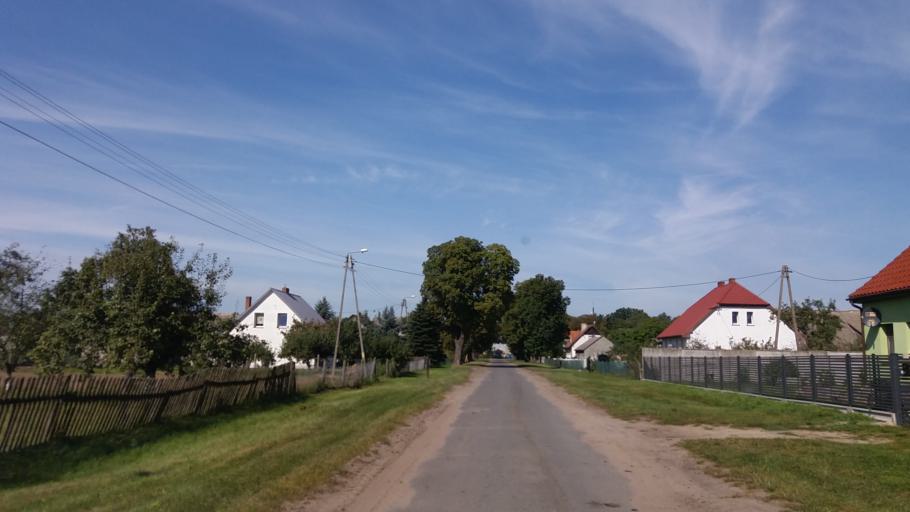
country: PL
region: West Pomeranian Voivodeship
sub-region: Powiat choszczenski
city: Choszczno
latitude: 53.1027
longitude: 15.4087
